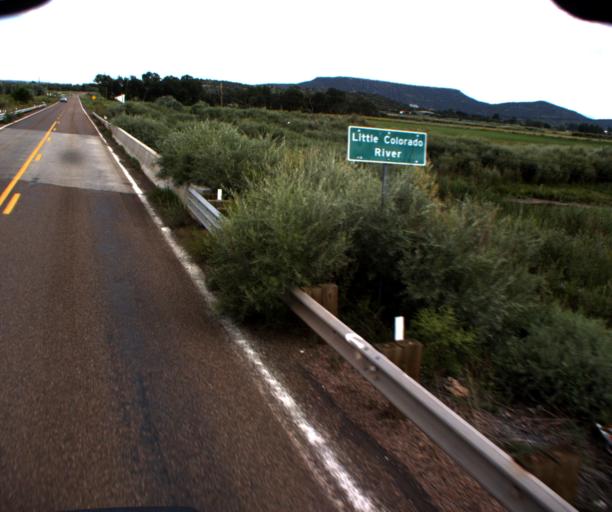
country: US
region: Arizona
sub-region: Apache County
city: Eagar
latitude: 34.1109
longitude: -109.3157
